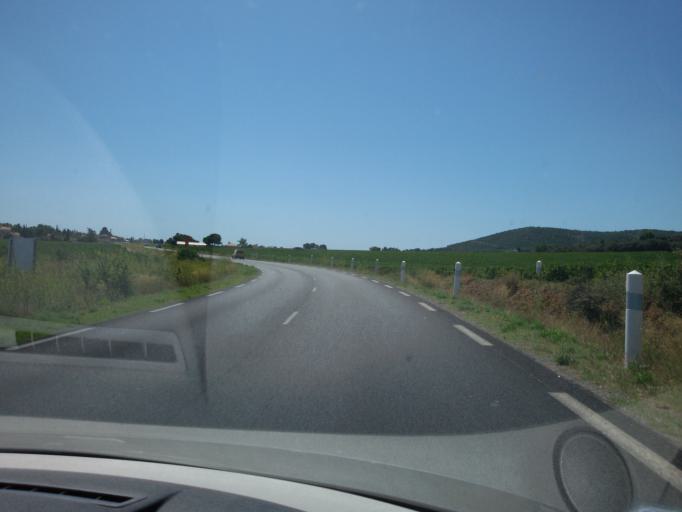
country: FR
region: Languedoc-Roussillon
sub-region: Departement de l'Herault
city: Vic-la-Gardiole
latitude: 43.4888
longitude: 3.7727
